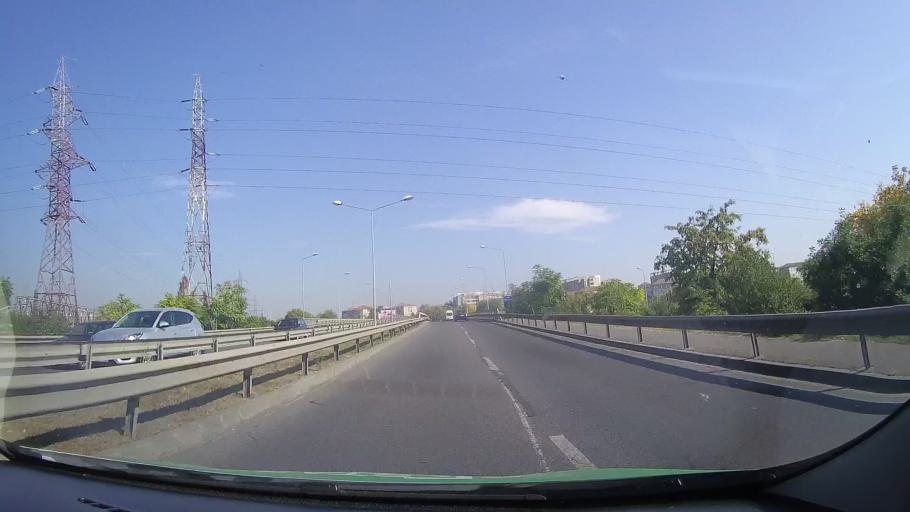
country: RO
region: Bihor
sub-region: Comuna Biharea
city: Oradea
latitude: 47.0708
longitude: 21.9039
